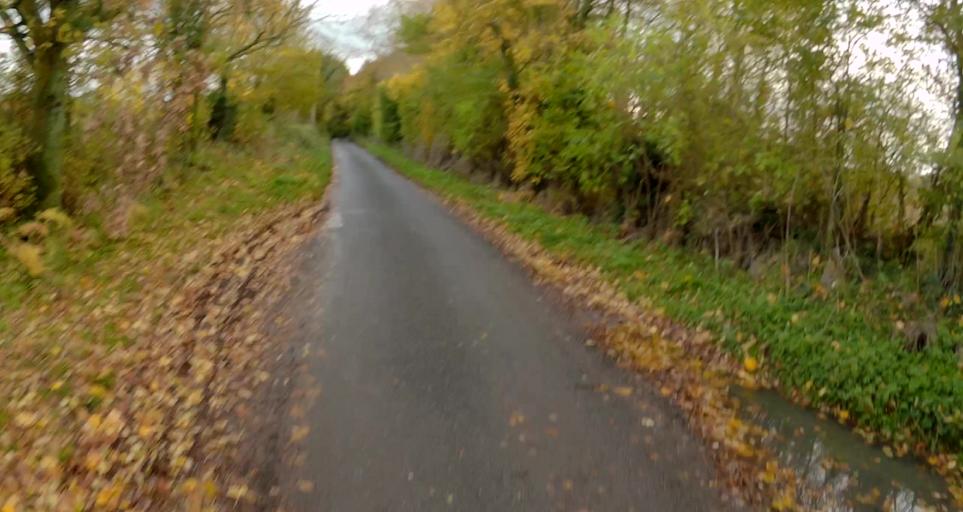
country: GB
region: England
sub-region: Hampshire
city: Long Sutton
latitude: 51.2152
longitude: -0.9632
